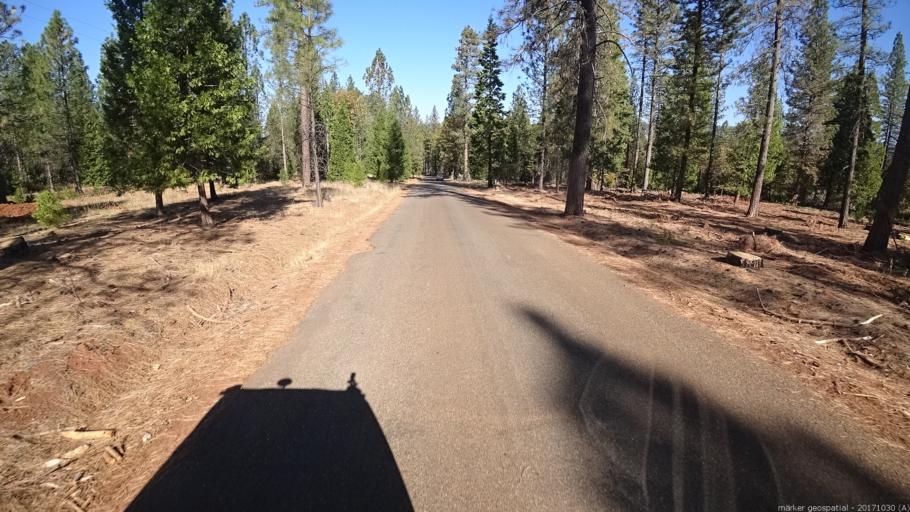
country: US
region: California
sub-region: Shasta County
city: Shingletown
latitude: 40.6269
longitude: -121.8950
